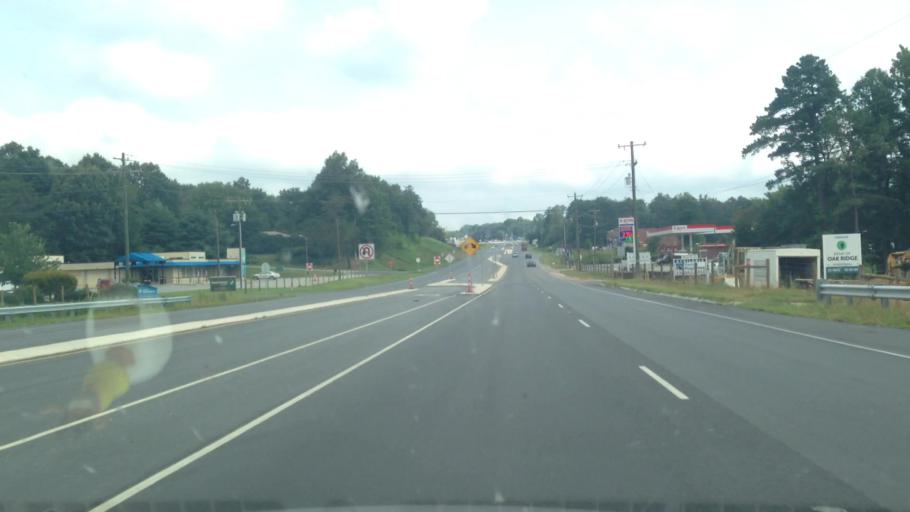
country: US
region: North Carolina
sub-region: Guilford County
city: Summerfield
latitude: 36.1854
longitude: -79.8888
